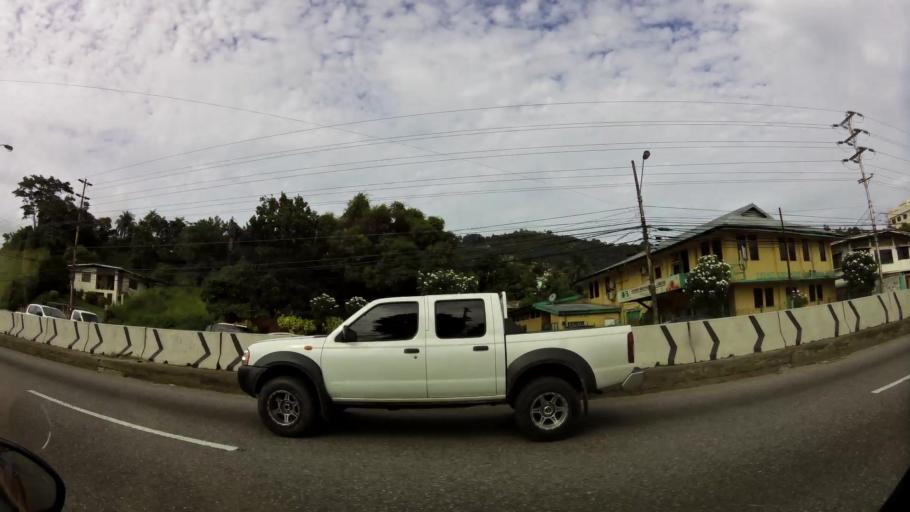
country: TT
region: City of Port of Spain
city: Mucurapo
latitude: 10.6779
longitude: -61.5486
